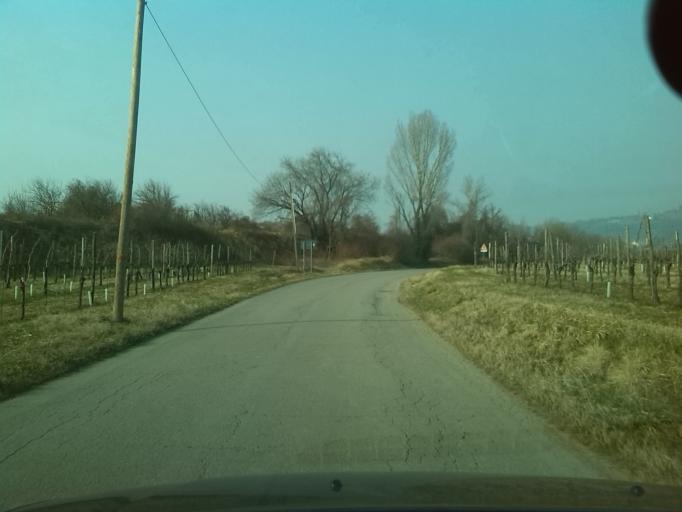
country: IT
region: Friuli Venezia Giulia
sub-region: Provincia di Gorizia
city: Cormons
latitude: 45.9430
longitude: 13.4723
